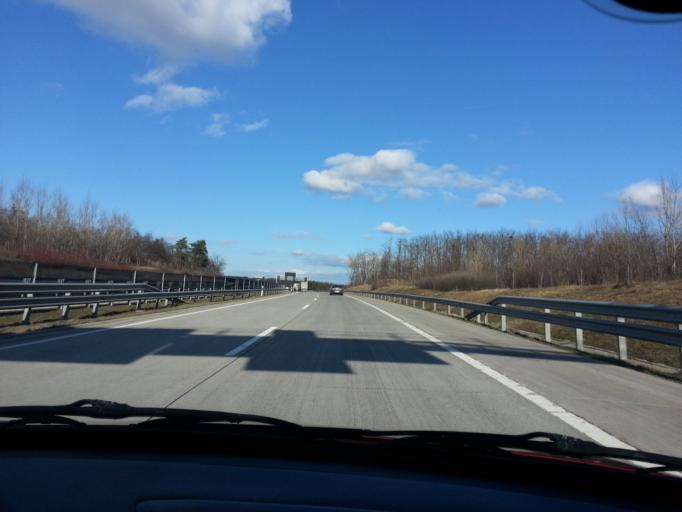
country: HU
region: Pest
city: Godollo
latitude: 47.5970
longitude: 19.3198
